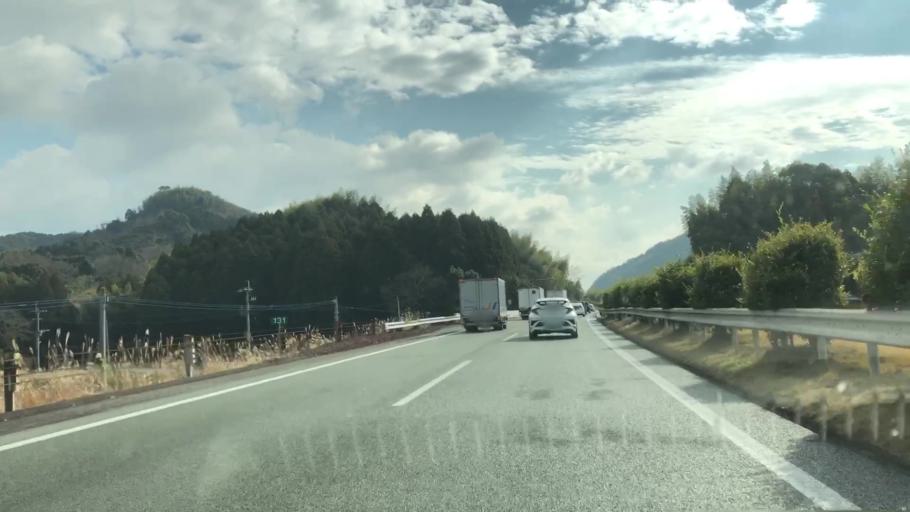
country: JP
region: Fukuoka
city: Setakamachi-takayanagi
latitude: 33.1067
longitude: 130.5339
